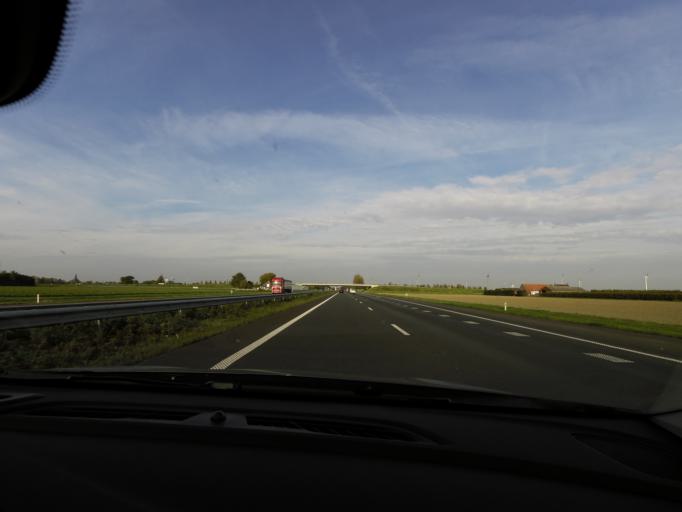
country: NL
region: North Brabant
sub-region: Gemeente Steenbergen
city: Dinteloord
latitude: 51.6213
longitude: 4.3796
